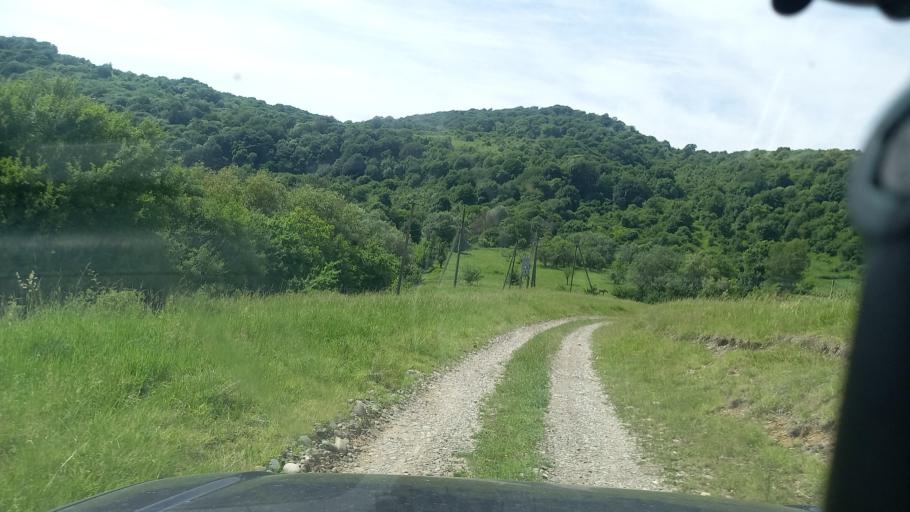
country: RU
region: Karachayevo-Cherkesiya
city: Kurdzhinovo
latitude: 44.1430
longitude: 41.0570
